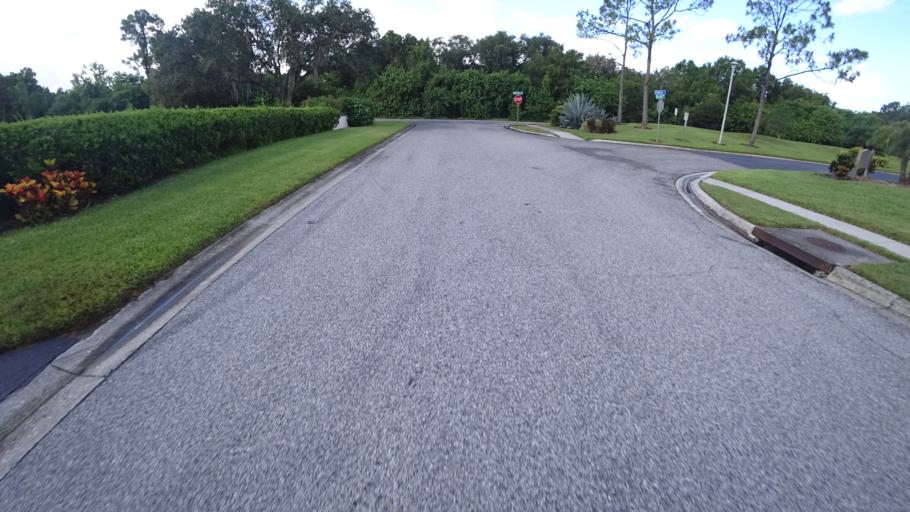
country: US
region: Florida
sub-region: Sarasota County
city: Desoto Lakes
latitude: 27.3934
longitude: -82.4827
